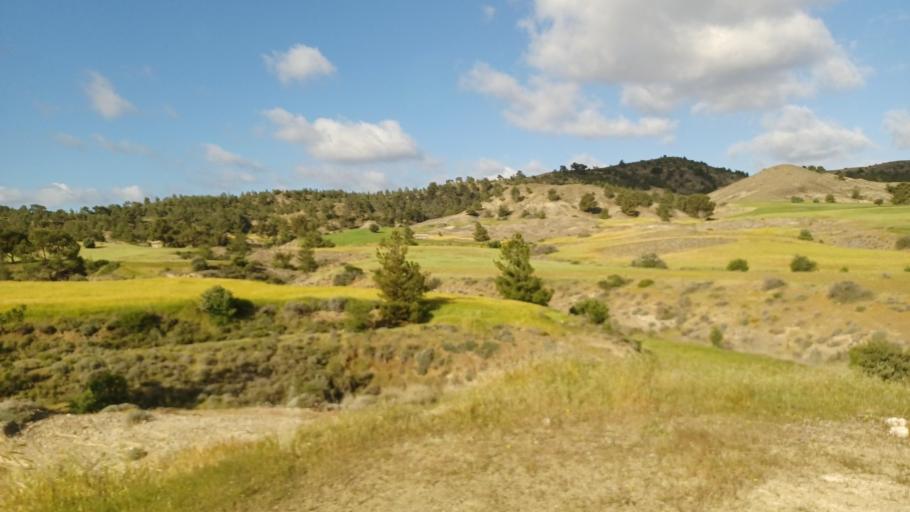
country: CY
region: Lefkosia
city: Peristerona
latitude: 35.0685
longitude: 33.0466
